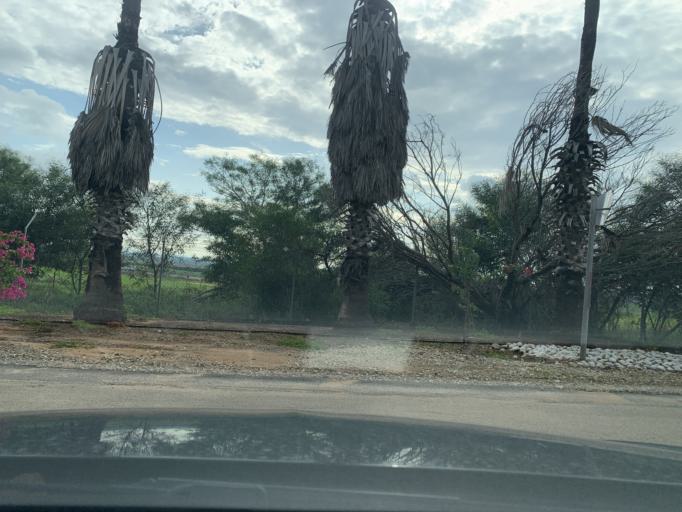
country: PS
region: West Bank
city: Qalqilyah
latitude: 32.1957
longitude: 34.9453
